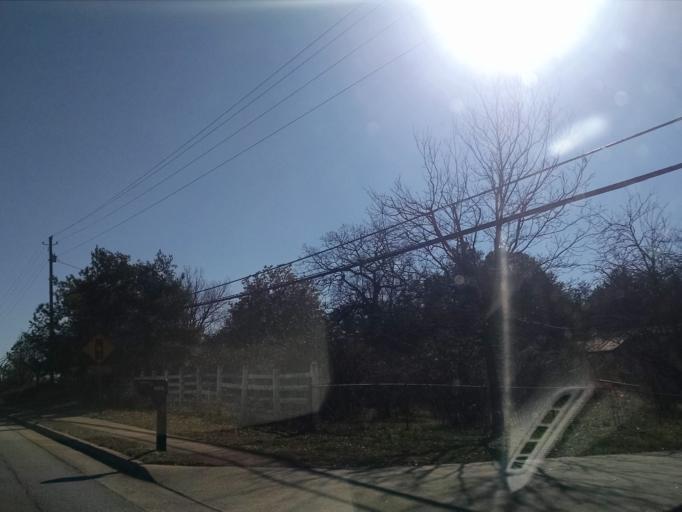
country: US
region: Georgia
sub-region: Gwinnett County
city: Suwanee
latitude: 34.0863
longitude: -84.0732
